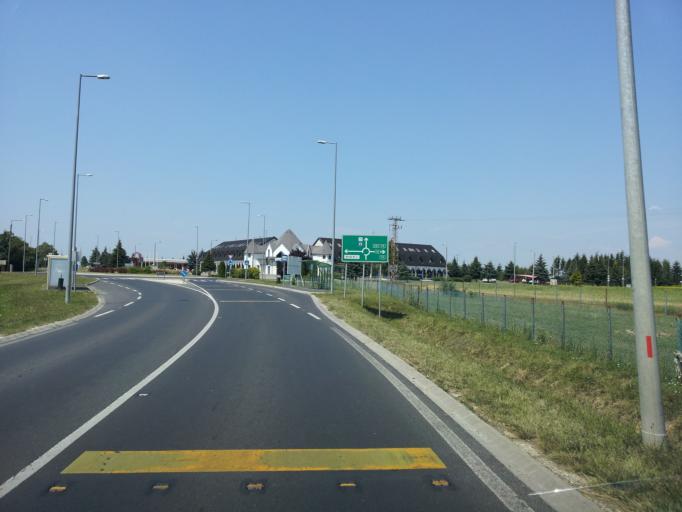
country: HU
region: Zala
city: Zalaegerszeg
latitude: 46.8681
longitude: 16.7958
